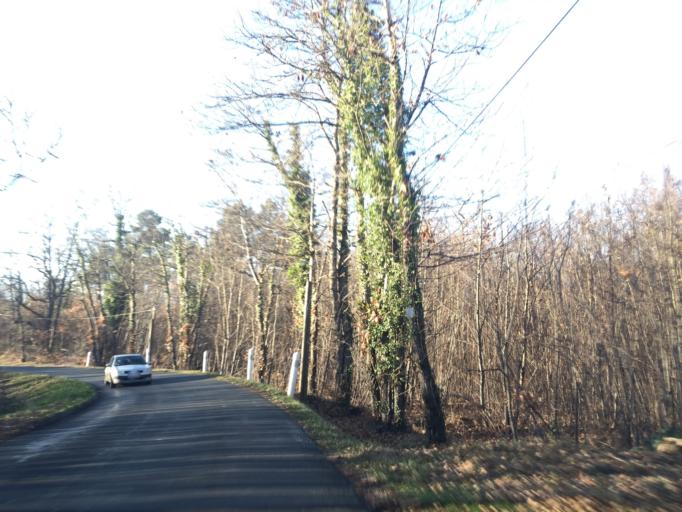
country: FR
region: Aquitaine
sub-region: Departement de la Dordogne
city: Riberac
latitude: 45.2039
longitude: 0.3495
